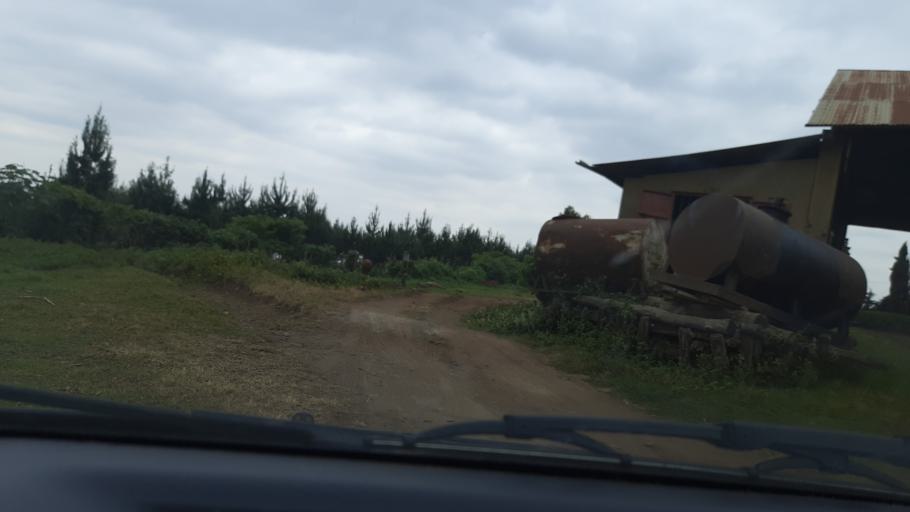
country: TZ
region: Kilimanjaro
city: Moshi
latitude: -2.9299
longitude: 37.4650
